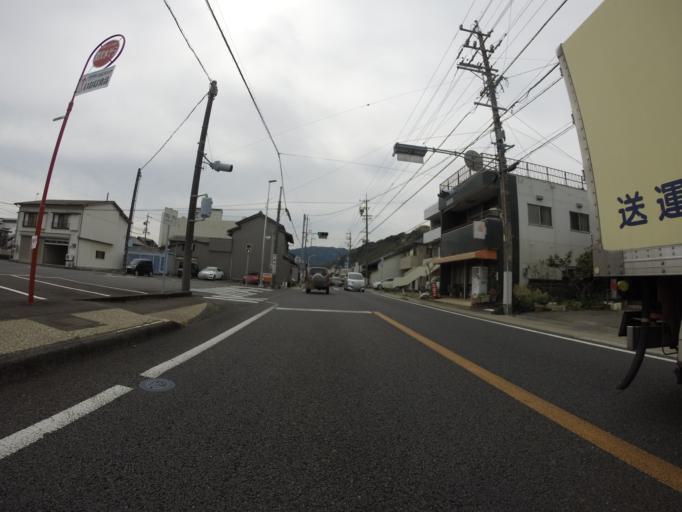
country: JP
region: Shizuoka
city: Fujinomiya
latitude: 35.1148
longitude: 138.5831
